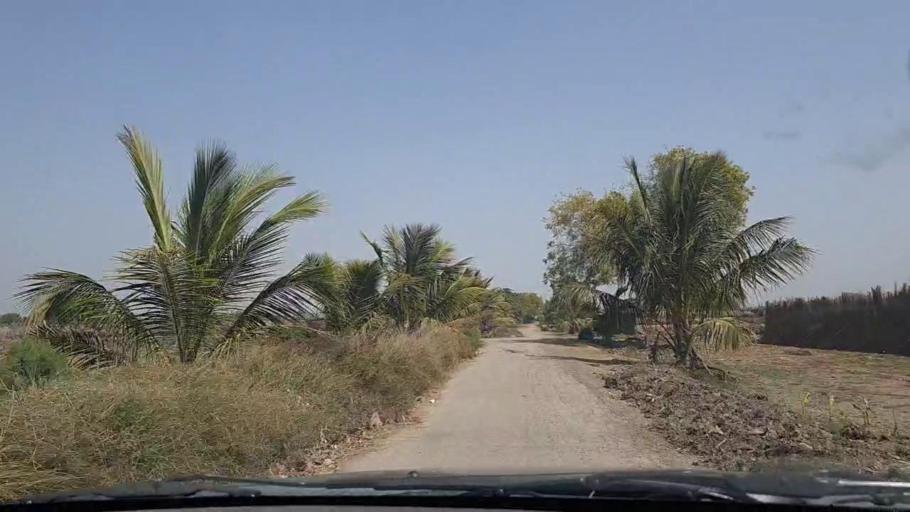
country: PK
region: Sindh
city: Keti Bandar
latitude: 24.2846
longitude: 67.6737
